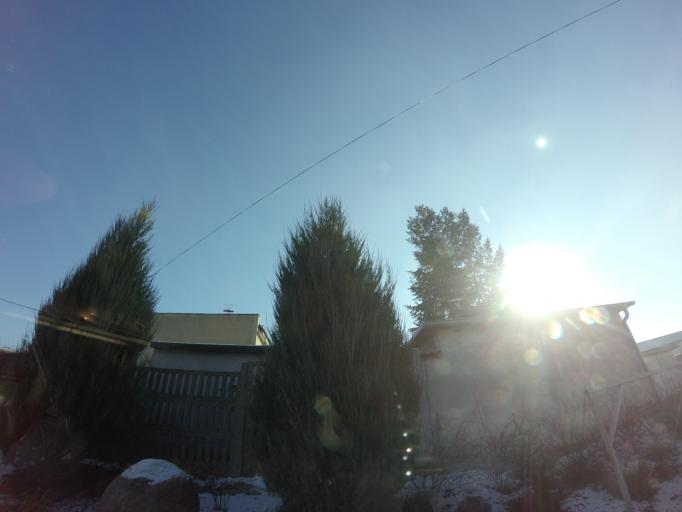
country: PL
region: West Pomeranian Voivodeship
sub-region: Powiat mysliborski
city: Barlinek
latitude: 52.9952
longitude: 15.2237
